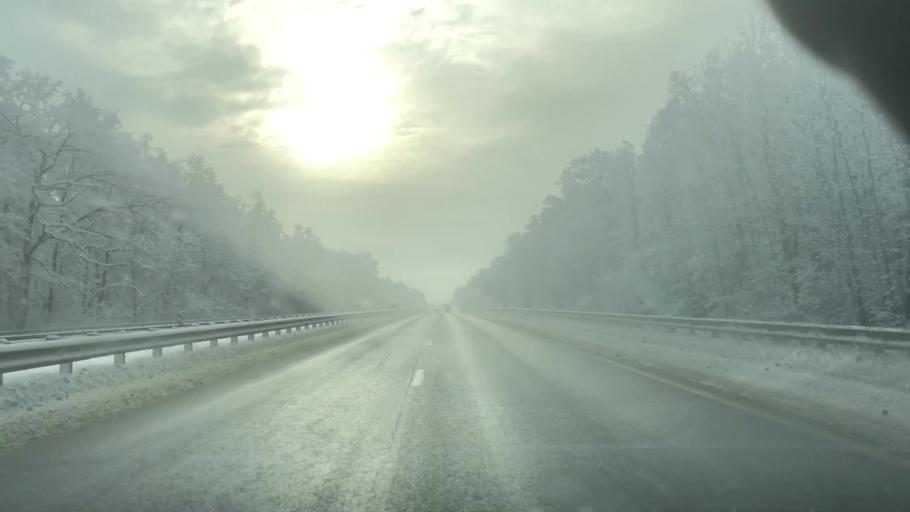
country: RU
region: Tula
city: Venev
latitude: 54.3670
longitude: 38.1547
